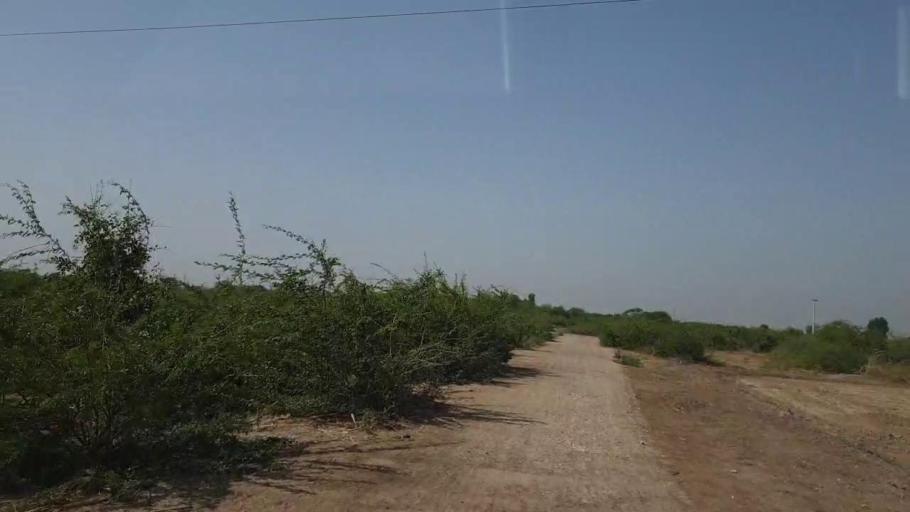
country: PK
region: Sindh
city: Naukot
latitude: 24.9904
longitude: 69.4752
